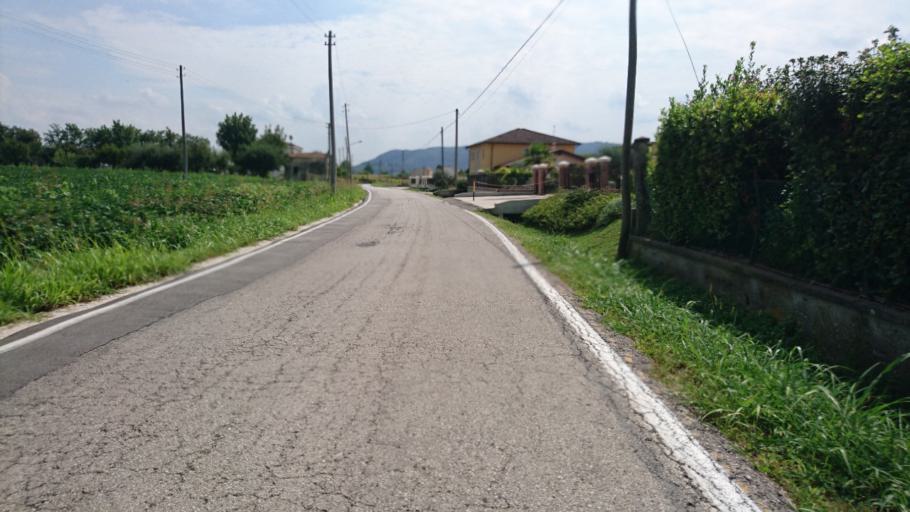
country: IT
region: Veneto
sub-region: Provincia di Vicenza
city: Arcugnano-Torri
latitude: 45.5112
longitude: 11.5837
